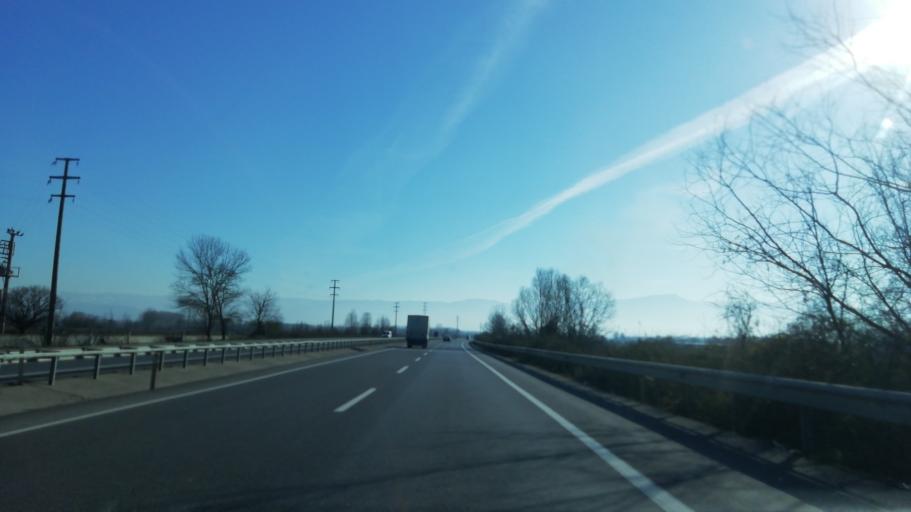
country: TR
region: Sakarya
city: Akyazi
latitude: 40.7383
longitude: 30.5646
